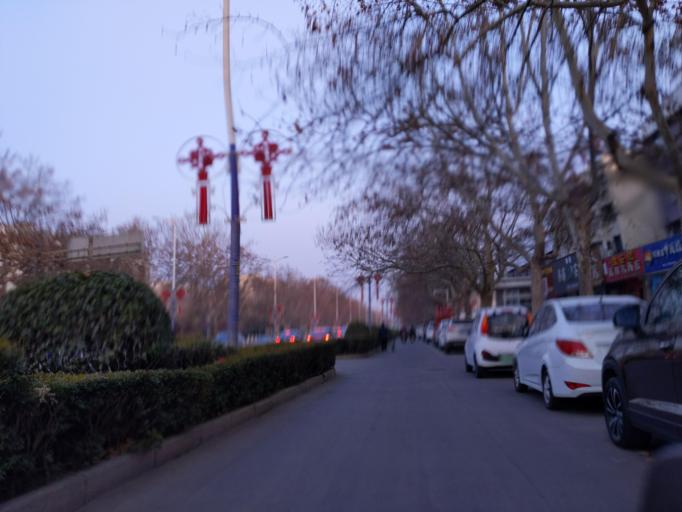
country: CN
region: Henan Sheng
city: Zhongyuanlu
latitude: 35.7741
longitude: 115.0872
